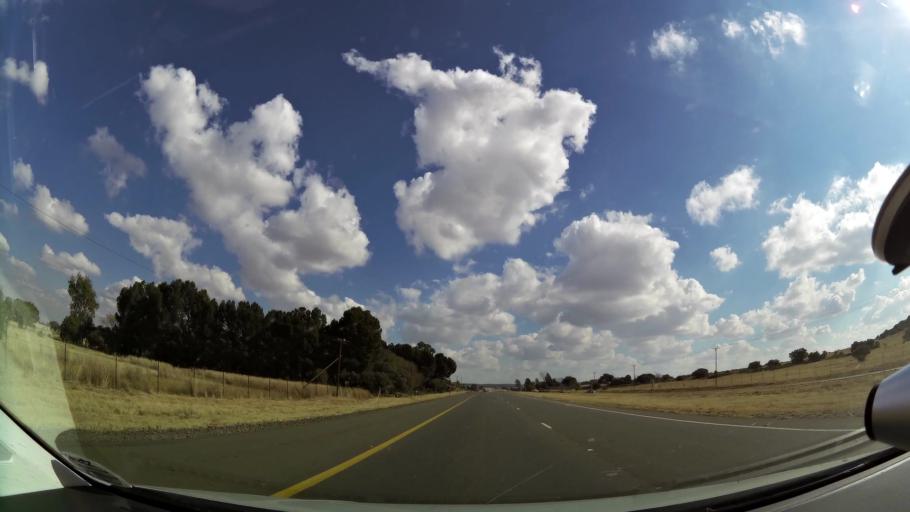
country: ZA
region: Orange Free State
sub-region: Mangaung Metropolitan Municipality
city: Bloemfontein
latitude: -29.1388
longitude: 26.1149
